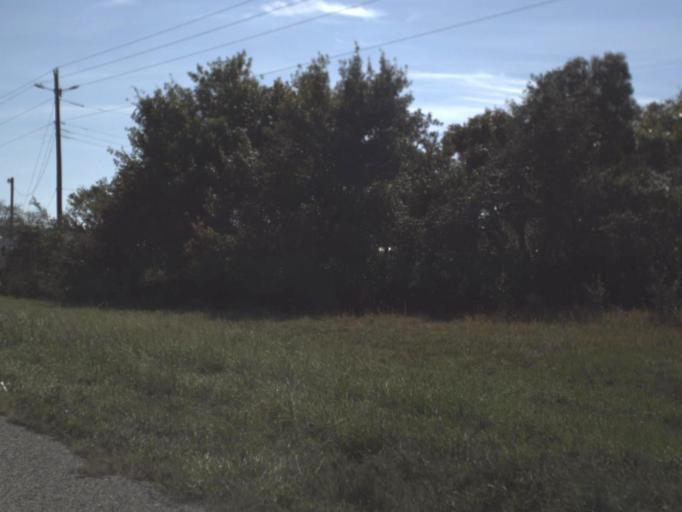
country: US
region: Florida
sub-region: Highlands County
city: Sebring
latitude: 27.3965
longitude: -81.4163
